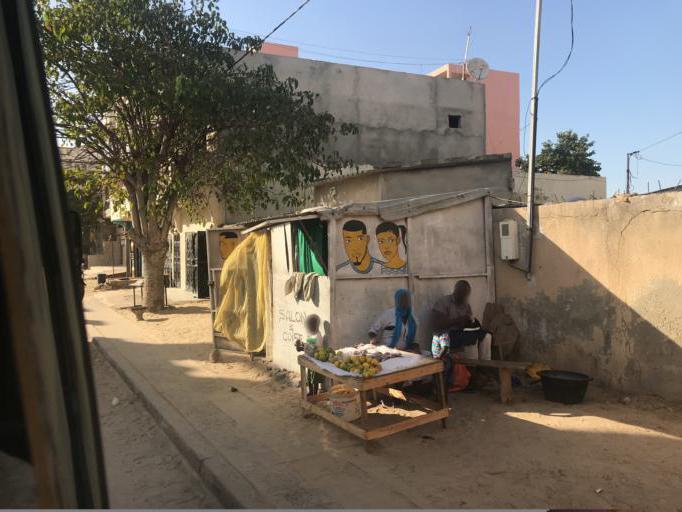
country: SN
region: Saint-Louis
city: Saint-Louis
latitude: 15.9933
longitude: -16.4887
